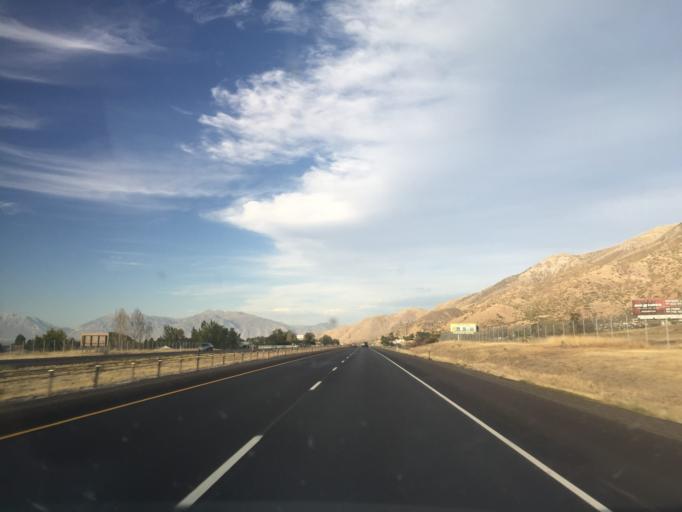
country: US
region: Utah
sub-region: Utah County
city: Santaquin
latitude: 39.9635
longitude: -111.7882
